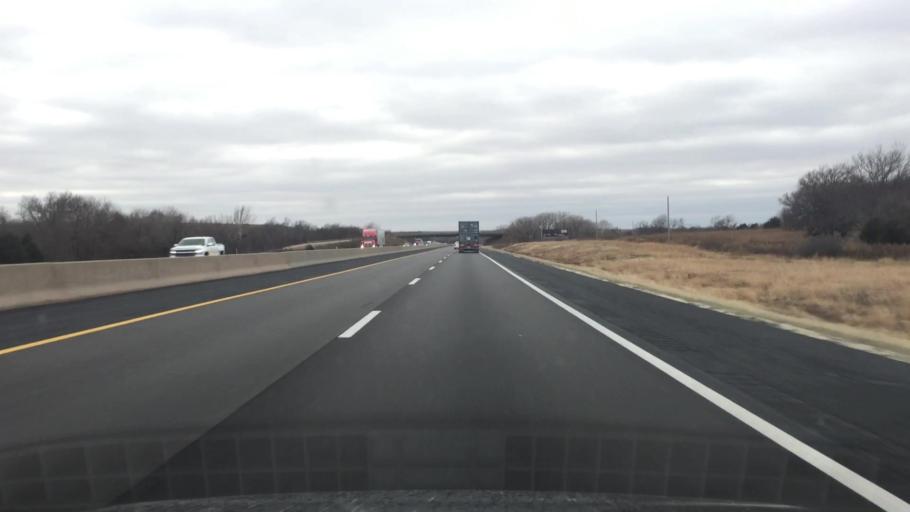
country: US
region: Kansas
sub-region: Chase County
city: Cottonwood Falls
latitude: 38.1466
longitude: -96.5084
